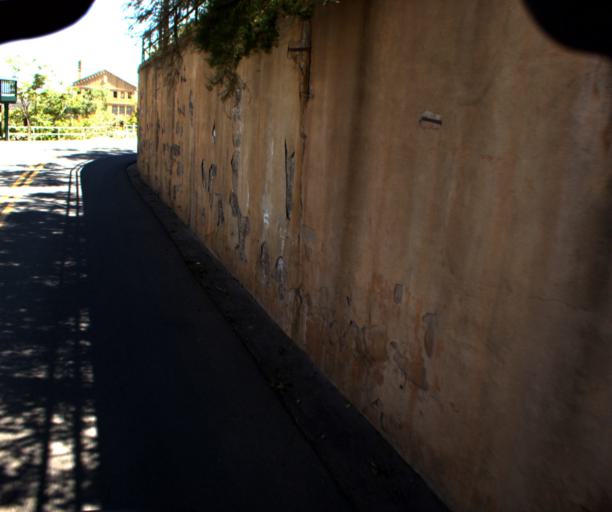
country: US
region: Arizona
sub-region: Yavapai County
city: Clarkdale
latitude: 34.7496
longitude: -112.1155
